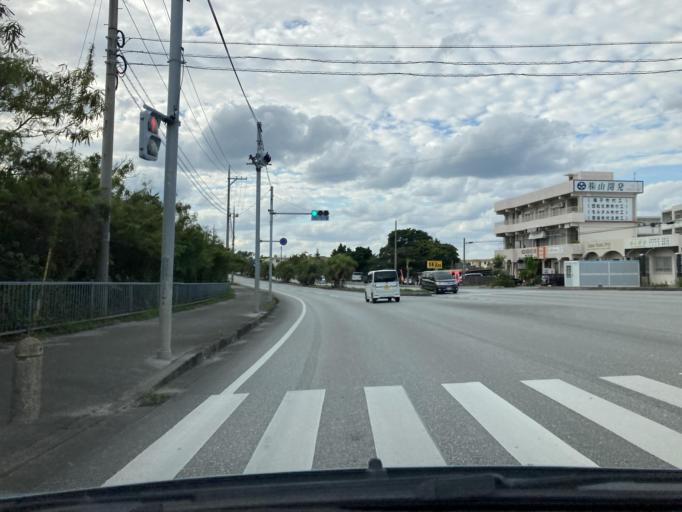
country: JP
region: Okinawa
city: Okinawa
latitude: 26.3597
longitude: 127.7997
